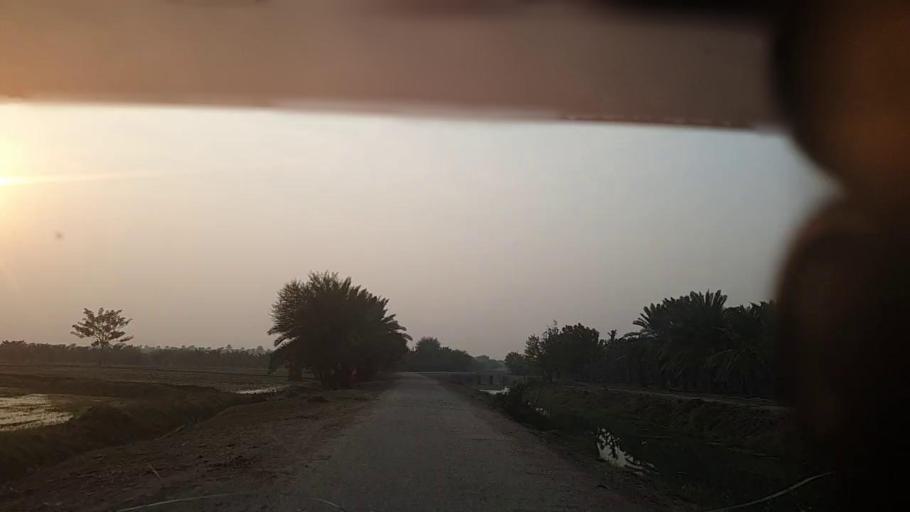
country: PK
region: Sindh
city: Pir jo Goth
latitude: 27.5214
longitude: 68.6474
